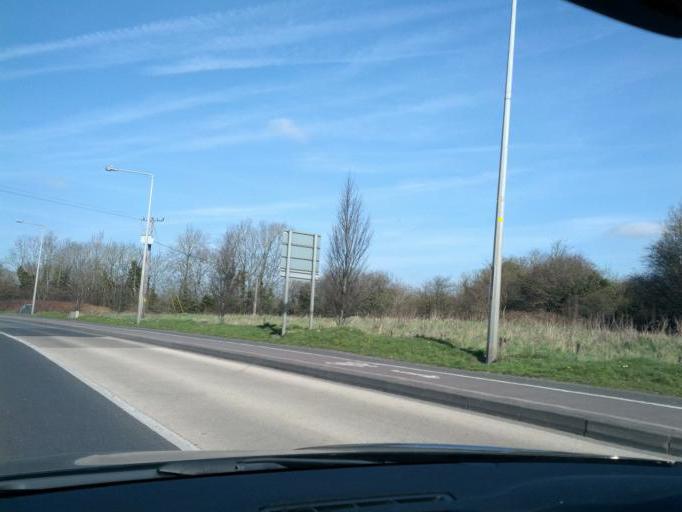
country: IE
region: Leinster
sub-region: Kildare
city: Celbridge
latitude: 53.3558
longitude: -6.5471
